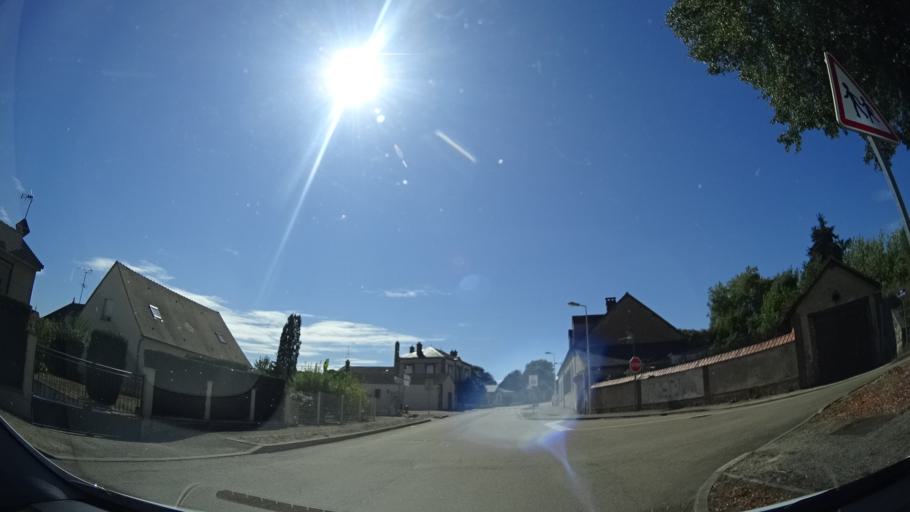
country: FR
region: Bourgogne
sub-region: Departement de l'Yonne
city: Charny
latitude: 47.9393
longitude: 3.1323
